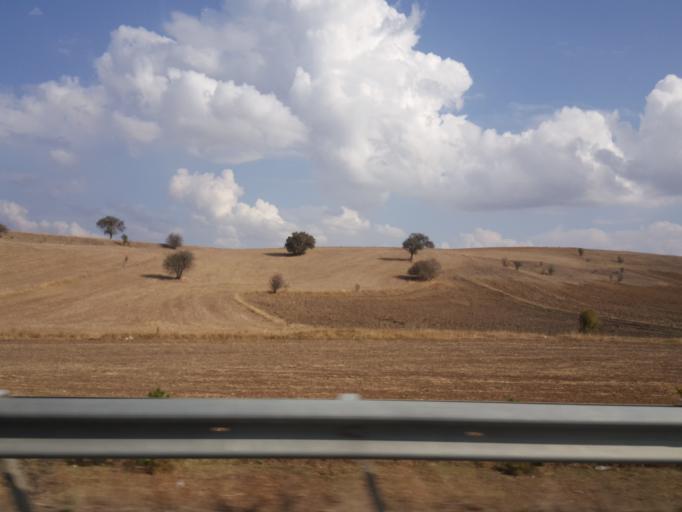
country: TR
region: Corum
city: Alaca
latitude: 40.3000
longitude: 34.6544
